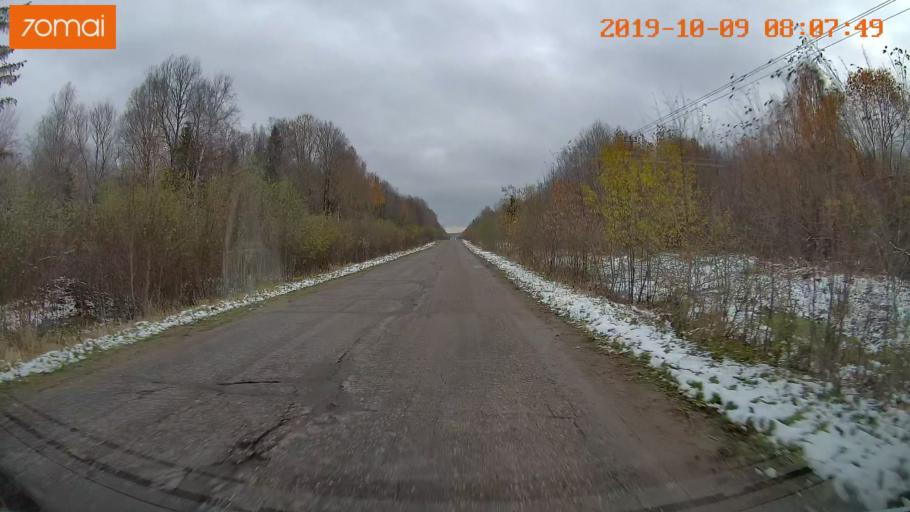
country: RU
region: Jaroslavl
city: Kukoboy
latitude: 58.7002
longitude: 40.0860
